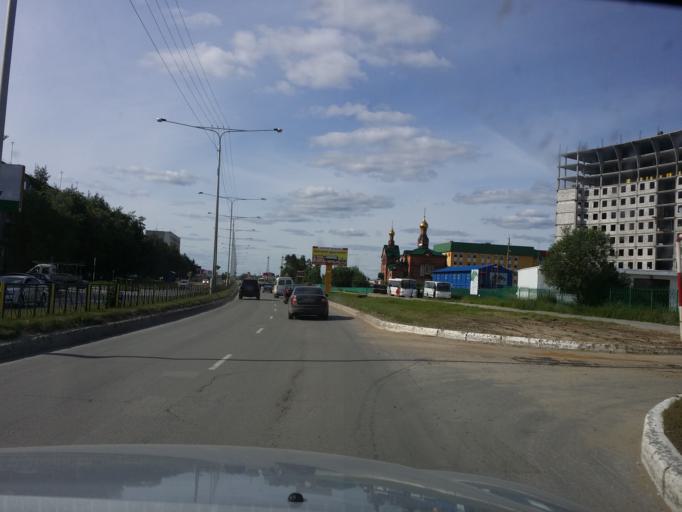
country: RU
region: Khanty-Mansiyskiy Avtonomnyy Okrug
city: Nizhnevartovsk
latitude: 60.9470
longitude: 76.5660
